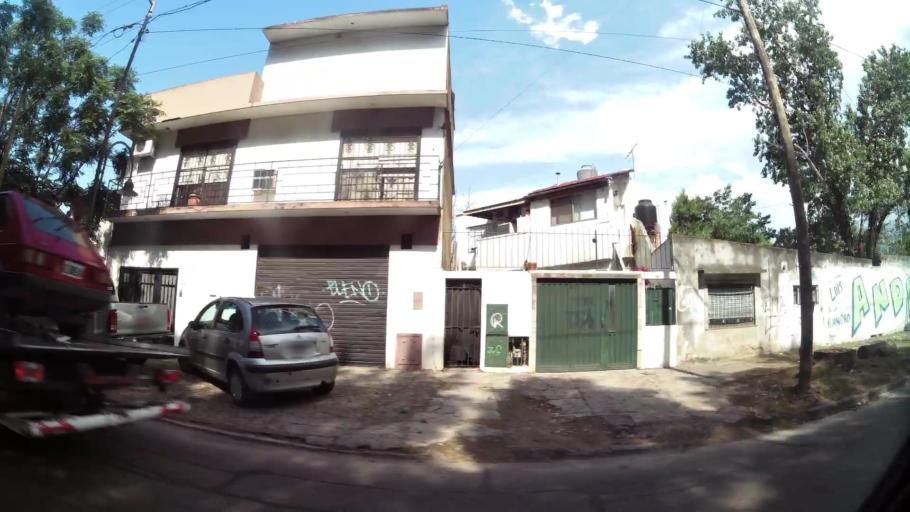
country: AR
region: Buenos Aires
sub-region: Partido de Tigre
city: Tigre
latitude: -34.4682
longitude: -58.5759
